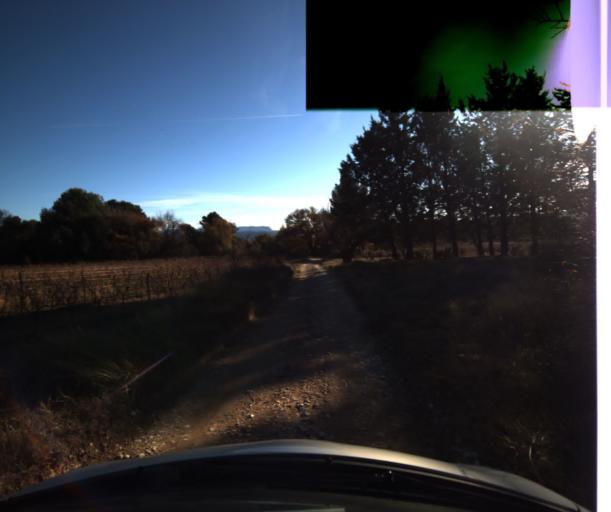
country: FR
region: Provence-Alpes-Cote d'Azur
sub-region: Departement du Vaucluse
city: Pertuis
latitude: 43.7051
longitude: 5.4812
